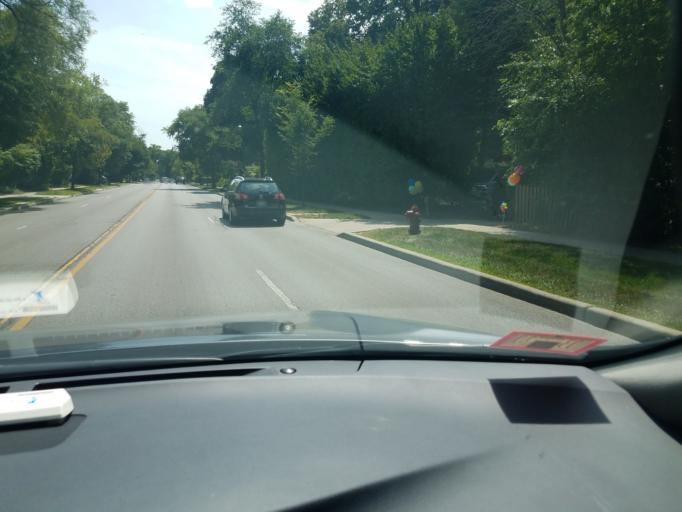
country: US
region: Illinois
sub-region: Cook County
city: Evanston
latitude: 42.0405
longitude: -87.6882
